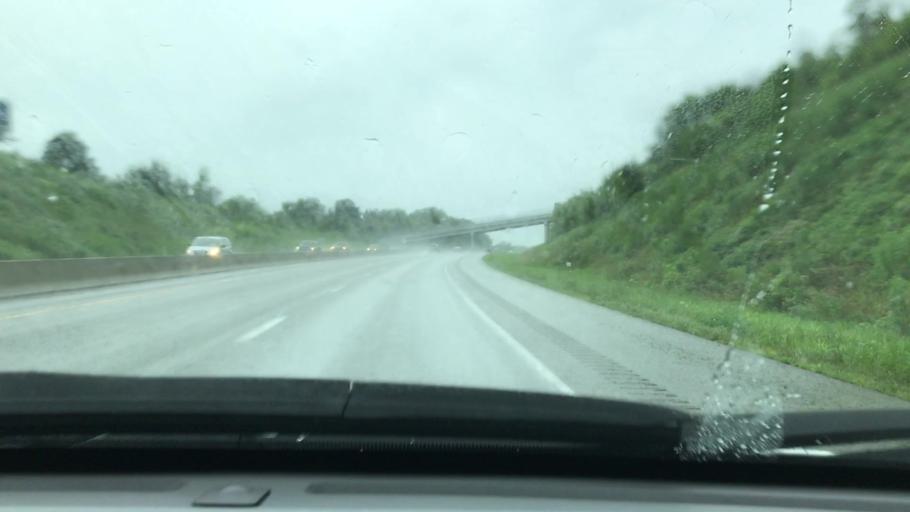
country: US
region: Pennsylvania
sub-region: Blair County
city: Tyrone
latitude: 40.6800
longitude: -78.2309
